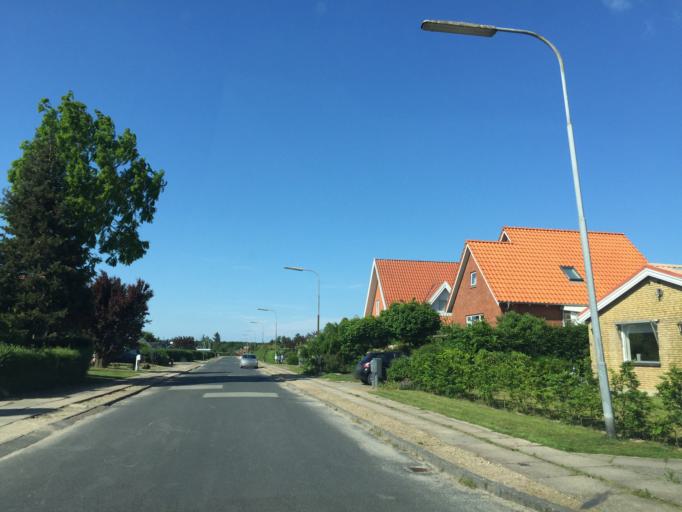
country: DK
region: South Denmark
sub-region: Odense Kommune
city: Odense
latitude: 55.3599
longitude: 10.3965
